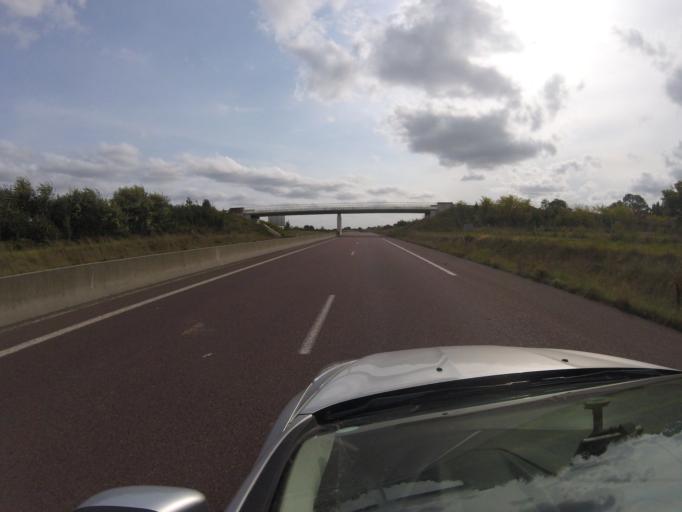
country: FR
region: Lower Normandy
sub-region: Departement de la Manche
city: Saint-Hilaire-Petitville
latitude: 49.2795
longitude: -1.1648
